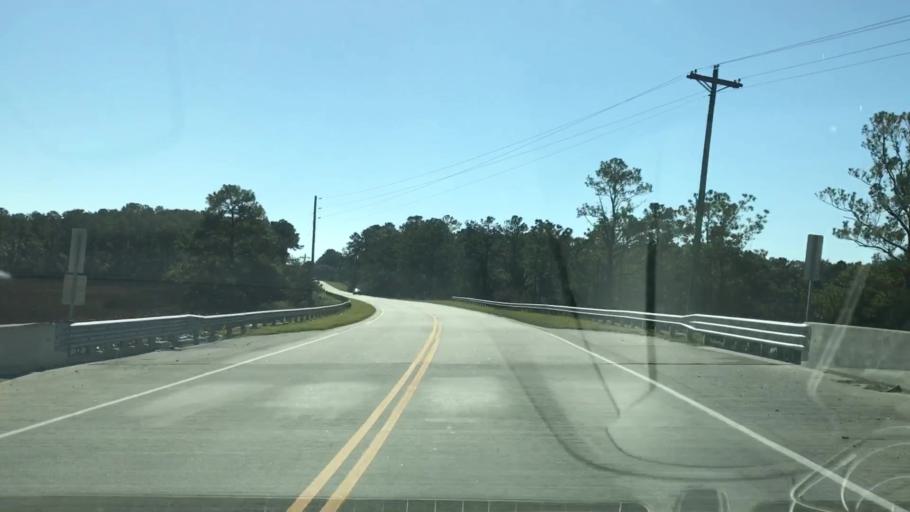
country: US
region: South Carolina
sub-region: Jasper County
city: Ridgeland
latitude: 32.4531
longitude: -80.8998
